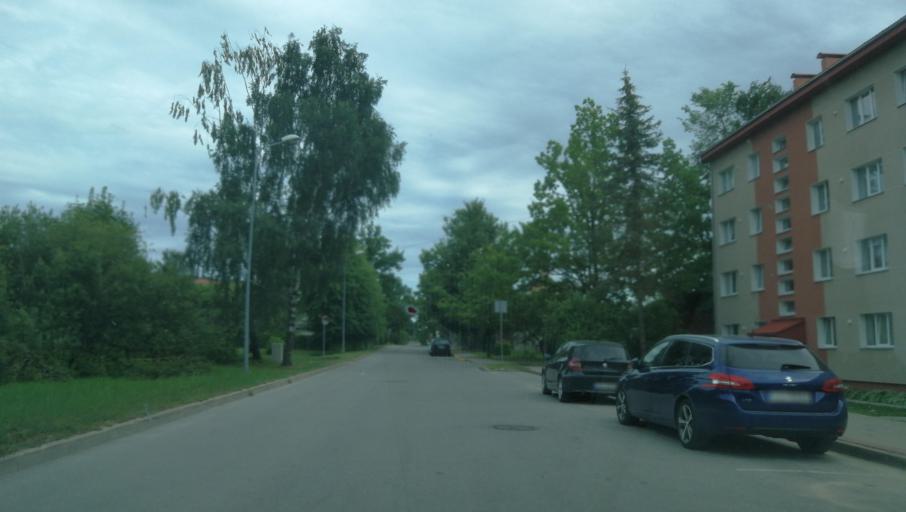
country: LV
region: Cesu Rajons
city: Cesis
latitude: 57.3034
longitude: 25.2810
